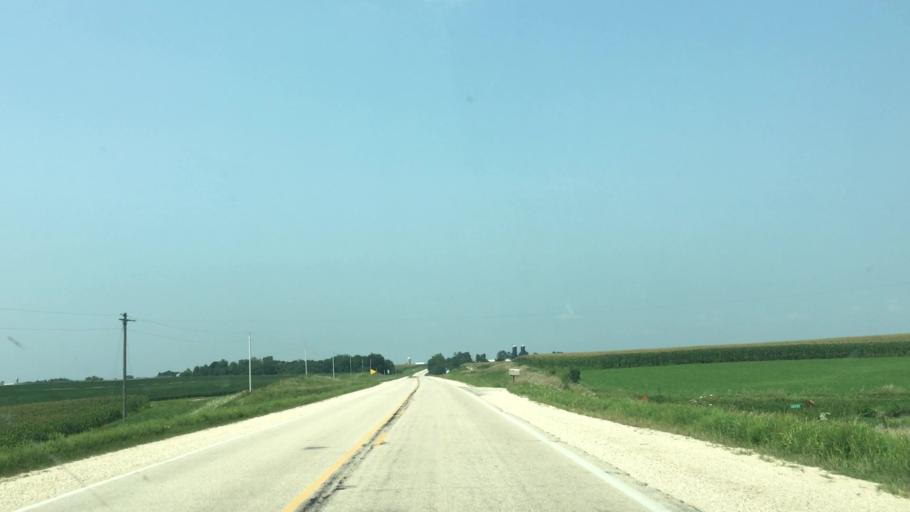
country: US
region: Iowa
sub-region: Fayette County
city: West Union
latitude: 42.9967
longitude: -91.8239
